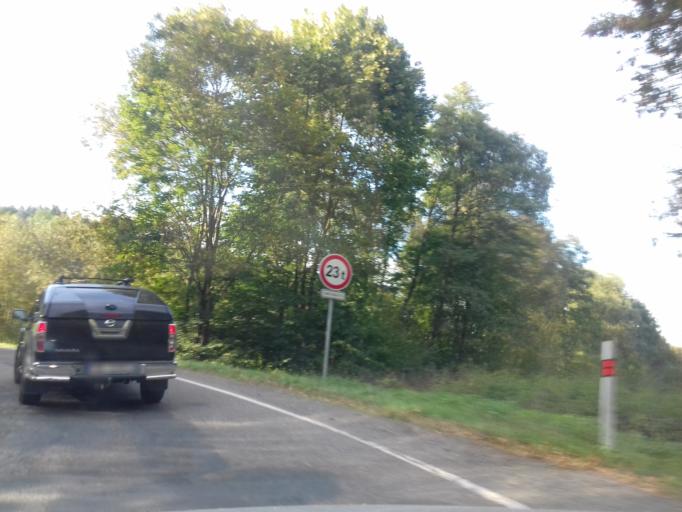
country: CZ
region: Central Bohemia
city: Neveklov
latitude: 49.7635
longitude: 14.5270
